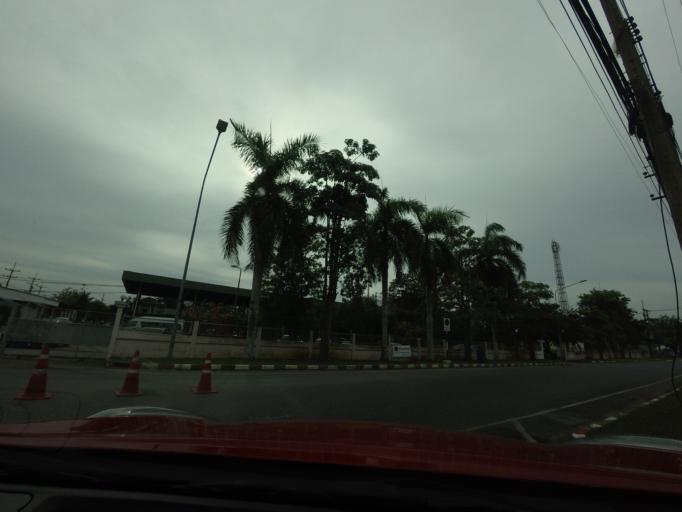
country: TH
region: Songkhla
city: Khlong Hoi Khong
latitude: 6.9369
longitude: 100.3925
